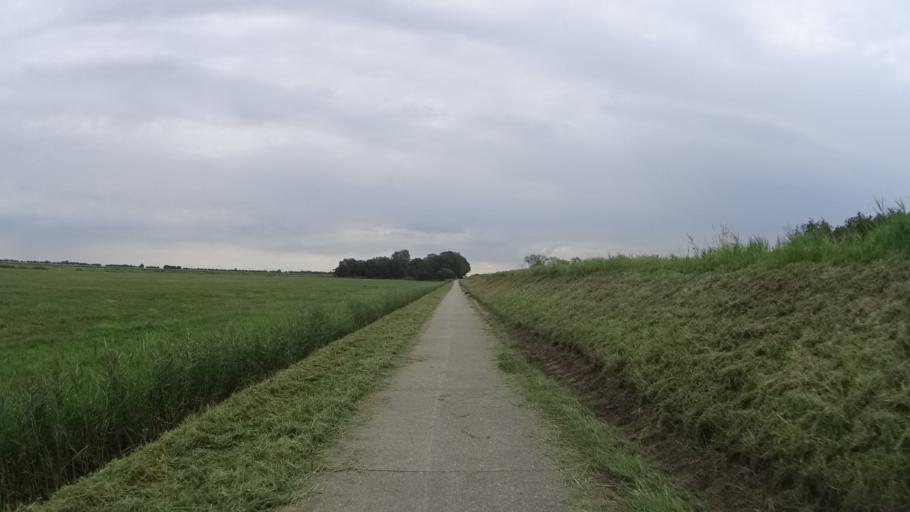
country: NL
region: Groningen
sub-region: Gemeente Haren
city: Haren
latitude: 53.2355
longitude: 6.6857
